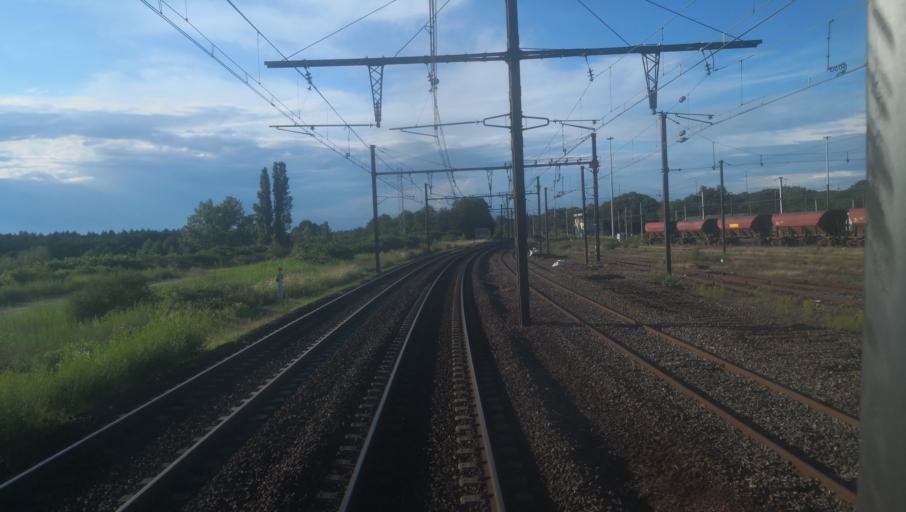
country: FR
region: Centre
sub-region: Departement du Cher
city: Vierzon
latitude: 47.2395
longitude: 2.0466
